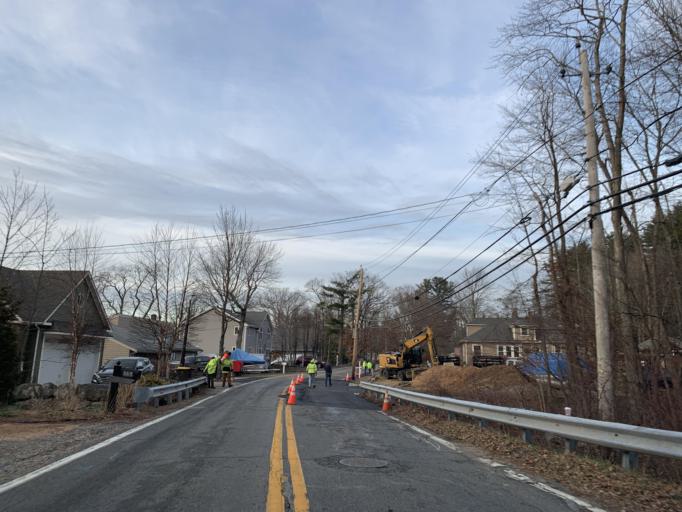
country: US
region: Rhode Island
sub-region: Providence County
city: Pascoag
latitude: 41.9387
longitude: -71.7047
